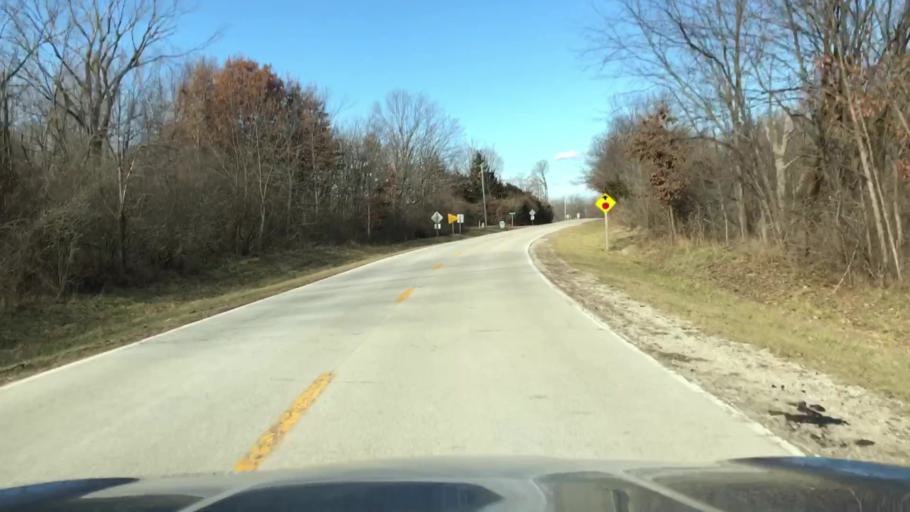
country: US
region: Illinois
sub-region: McLean County
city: Hudson
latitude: 40.6549
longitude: -88.9241
